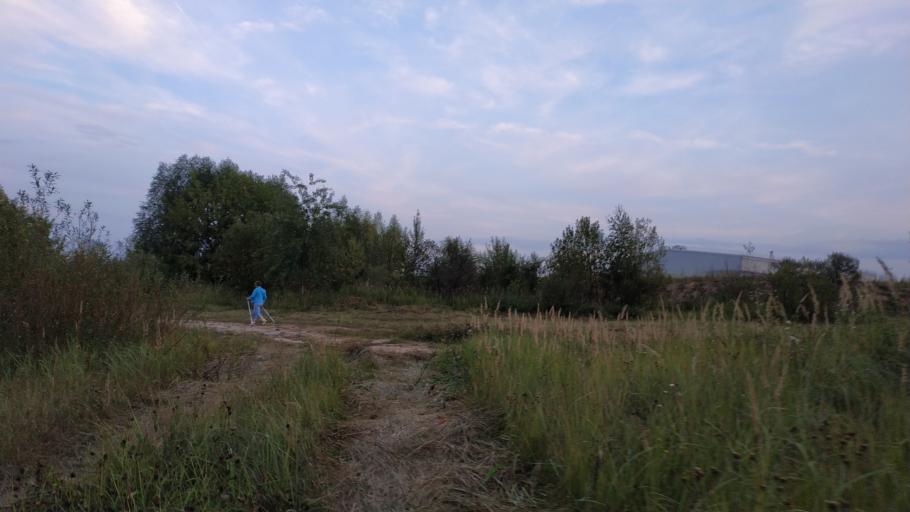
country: RU
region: Moscow
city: Solntsevo
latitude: 55.6394
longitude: 37.3717
